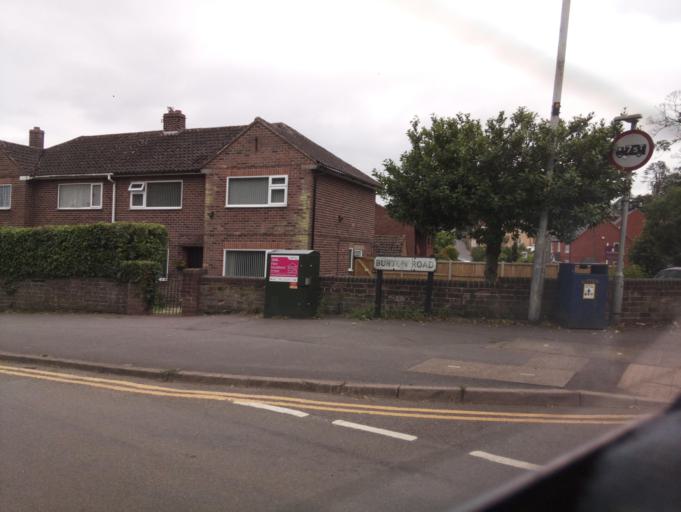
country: GB
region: England
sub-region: Leicestershire
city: Melton Mowbray
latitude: 52.7603
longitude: -0.8836
